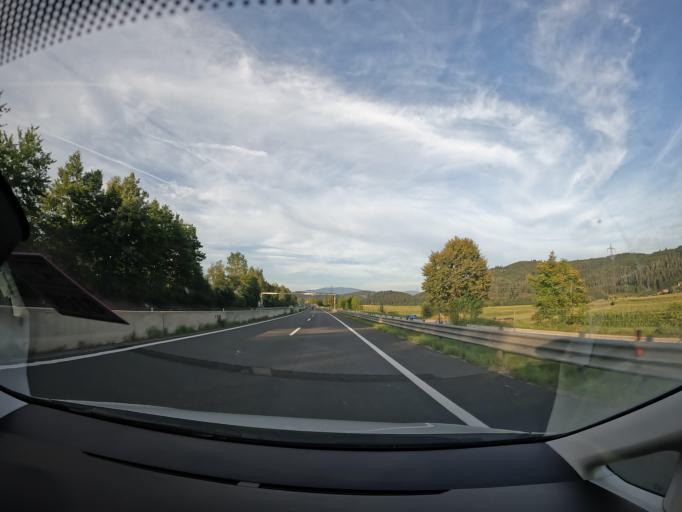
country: AT
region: Carinthia
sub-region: Politischer Bezirk Volkermarkt
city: Griffen
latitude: 46.6879
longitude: 14.7022
